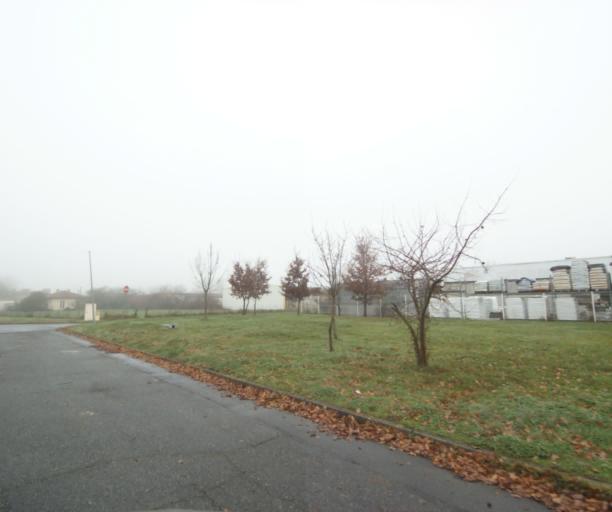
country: FR
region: Midi-Pyrenees
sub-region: Departement de la Haute-Garonne
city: Villemur-sur-Tarn
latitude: 43.8460
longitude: 1.4960
